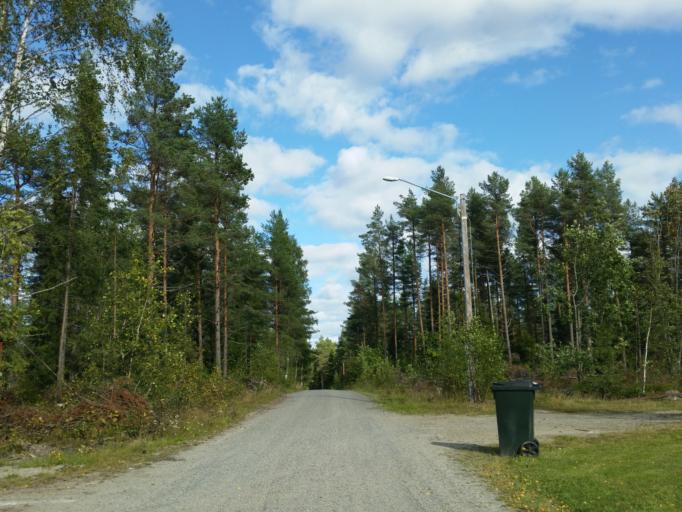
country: SE
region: Vaesterbotten
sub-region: Robertsfors Kommun
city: Robertsfors
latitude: 64.0457
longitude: 20.8649
